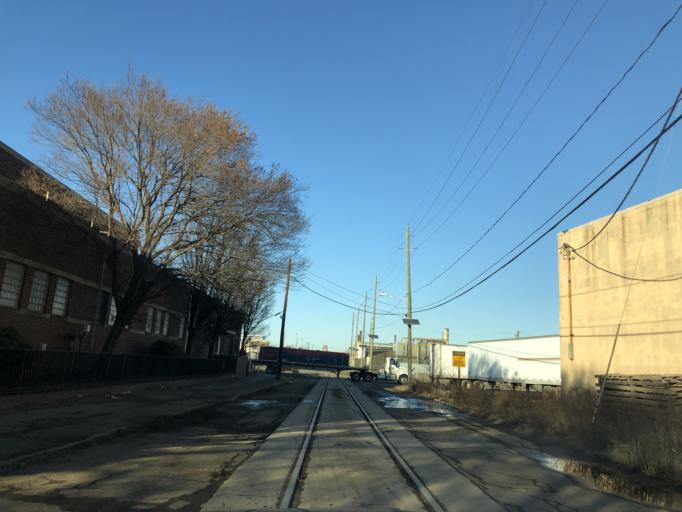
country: US
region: New Jersey
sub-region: Camden County
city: Camden
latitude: 39.9311
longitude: -75.1292
